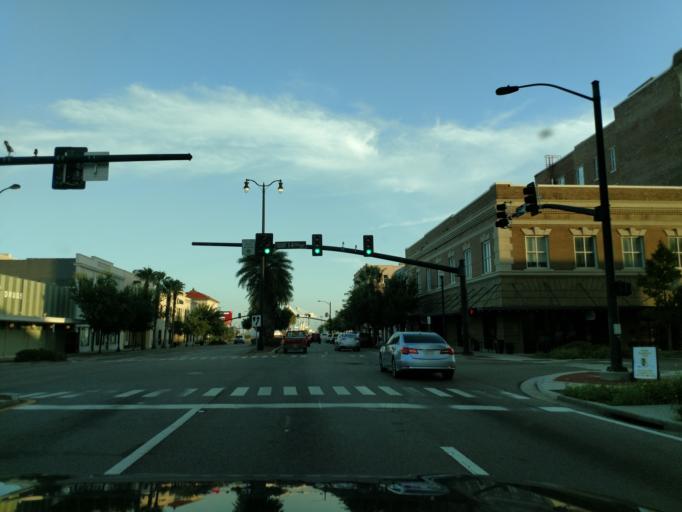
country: US
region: Mississippi
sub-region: Harrison County
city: Gulfport
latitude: 30.3685
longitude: -89.0930
